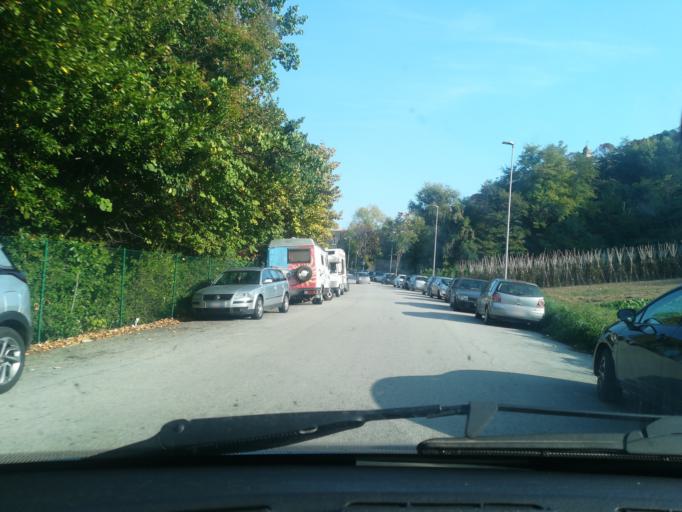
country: IT
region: The Marches
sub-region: Provincia di Macerata
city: Macerata
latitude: 43.3025
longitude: 13.4544
